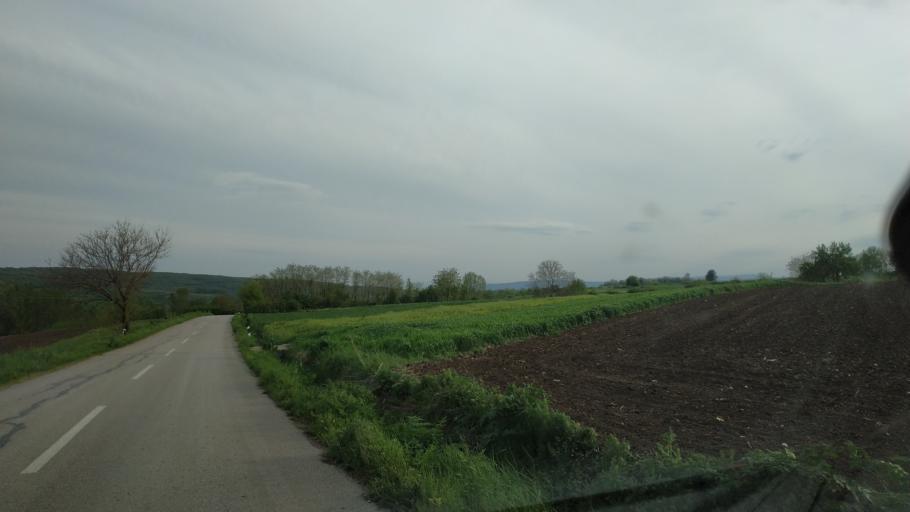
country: RS
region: Central Serbia
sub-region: Zajecarski Okrug
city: Soko Banja
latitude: 43.5219
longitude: 21.8481
